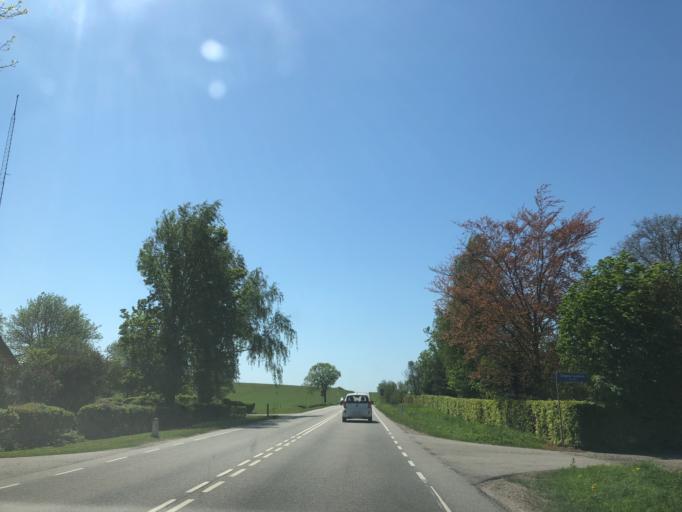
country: DK
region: Zealand
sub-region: Slagelse Kommune
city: Forlev
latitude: 55.3493
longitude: 11.2354
